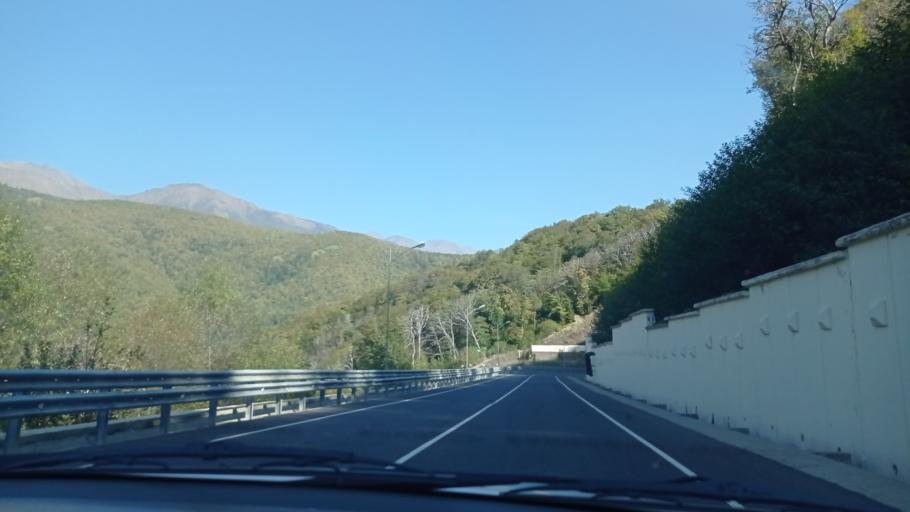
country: RU
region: Krasnodarskiy
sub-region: Sochi City
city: Krasnaya Polyana
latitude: 43.6807
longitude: 40.2435
